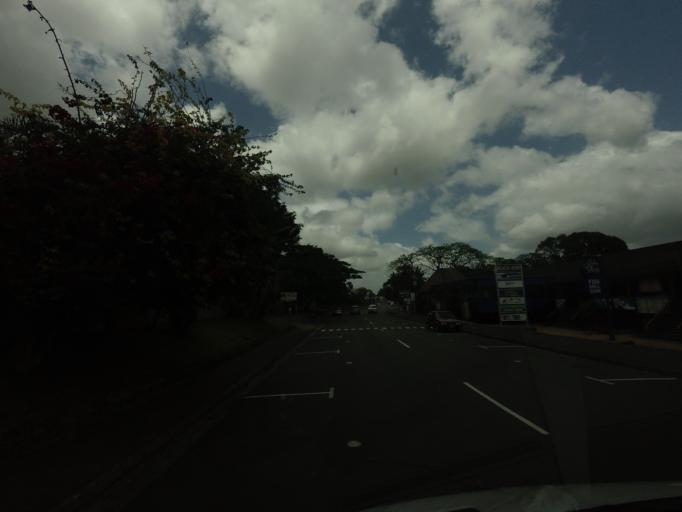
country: ZA
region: KwaZulu-Natal
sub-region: uMkhanyakude District Municipality
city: Mtubatuba
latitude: -28.3738
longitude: 32.4123
